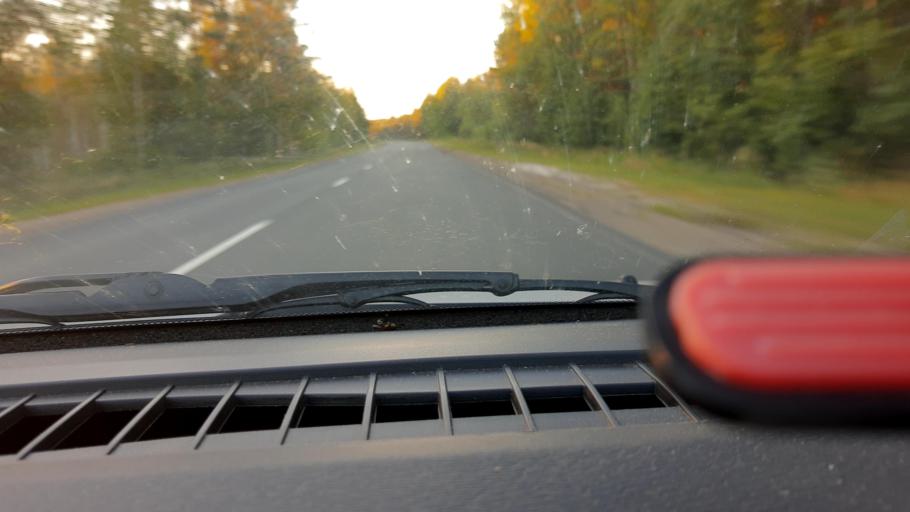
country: RU
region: Nizjnij Novgorod
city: Uren'
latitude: 57.3908
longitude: 45.6868
